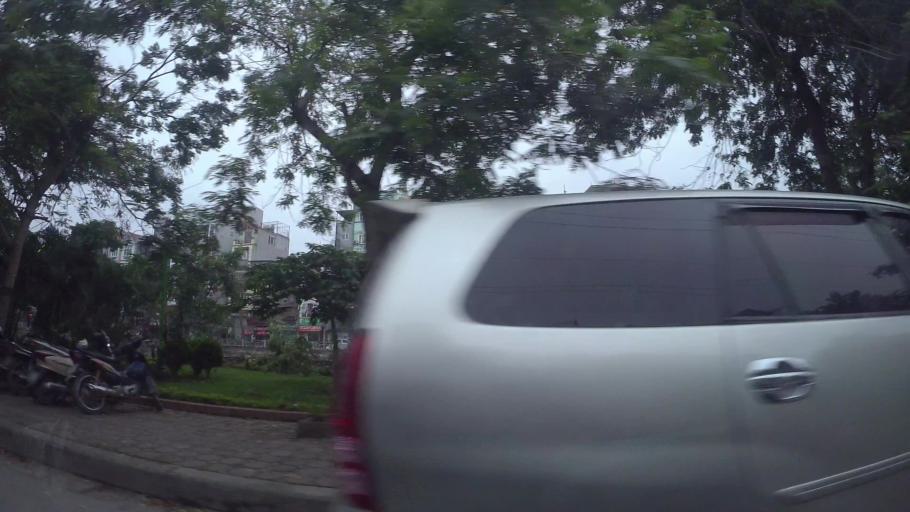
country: VN
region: Ha Noi
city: Hai BaTrung
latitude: 20.9884
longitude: 105.8440
